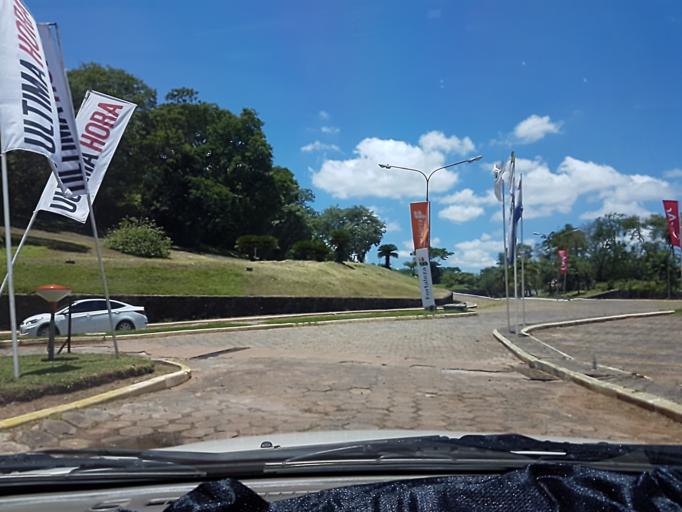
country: PY
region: Central
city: Lambare
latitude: -25.3433
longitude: -57.6427
